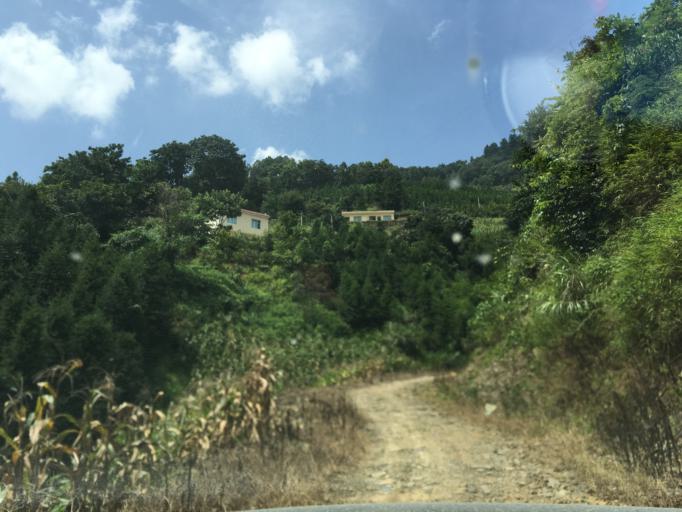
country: CN
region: Guangxi Zhuangzu Zizhiqu
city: Xinzhou
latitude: 24.9541
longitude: 105.7857
